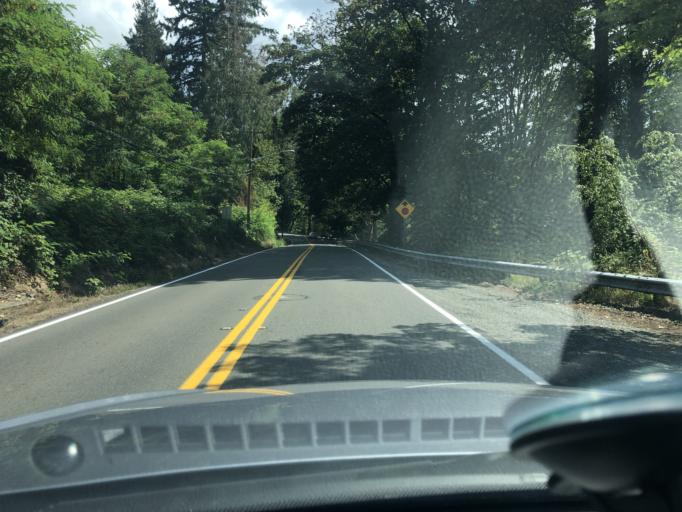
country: US
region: Washington
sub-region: King County
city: Lea Hill
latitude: 47.3270
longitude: -122.2040
